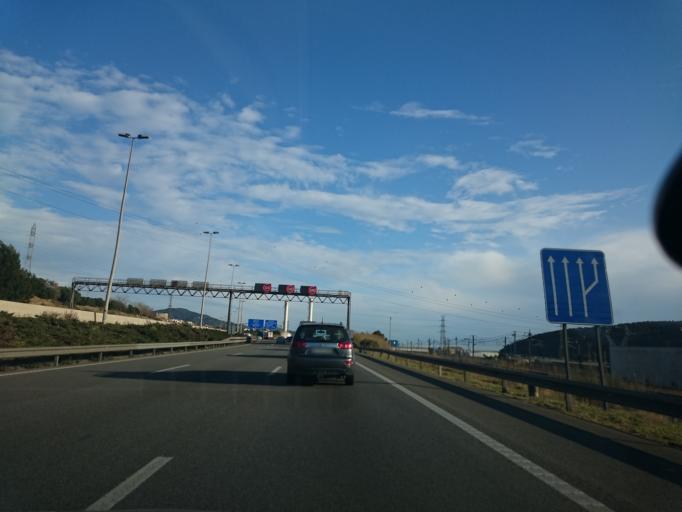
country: ES
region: Catalonia
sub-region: Provincia de Barcelona
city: Sant Andreu de la Barca
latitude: 41.4510
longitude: 1.9858
